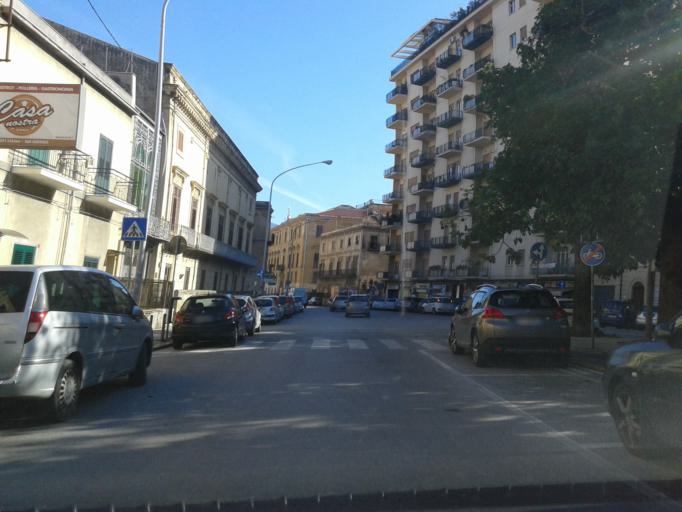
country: IT
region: Sicily
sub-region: Palermo
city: Palermo
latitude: 38.1195
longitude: 13.3416
